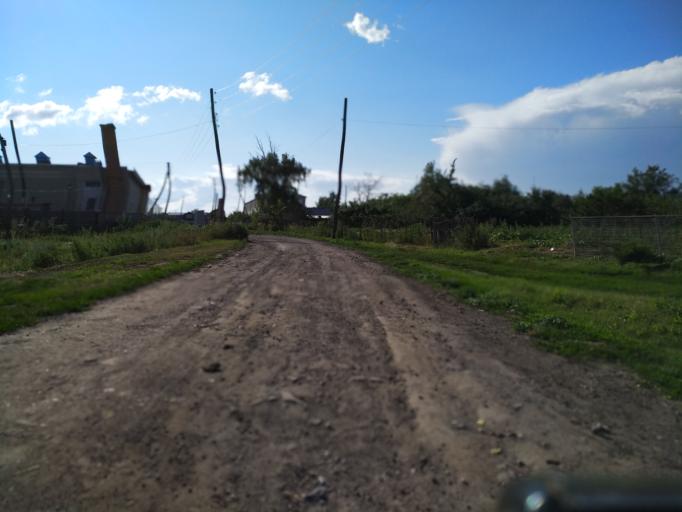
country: RU
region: Lipetsk
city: Dobrinka
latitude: 52.0373
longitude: 40.5566
